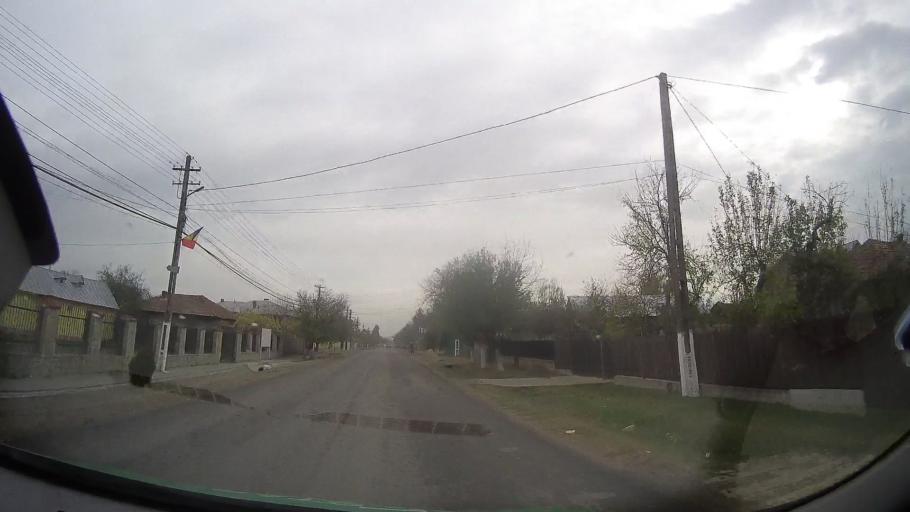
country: RO
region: Prahova
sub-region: Comuna Dumbrava
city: Dumbrava
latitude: 44.8730
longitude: 26.1899
